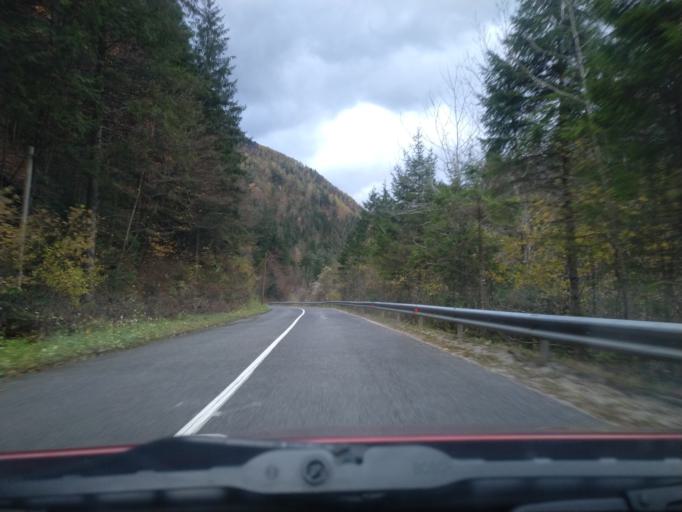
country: SI
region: Luce
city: Luce
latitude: 46.3840
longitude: 14.7242
